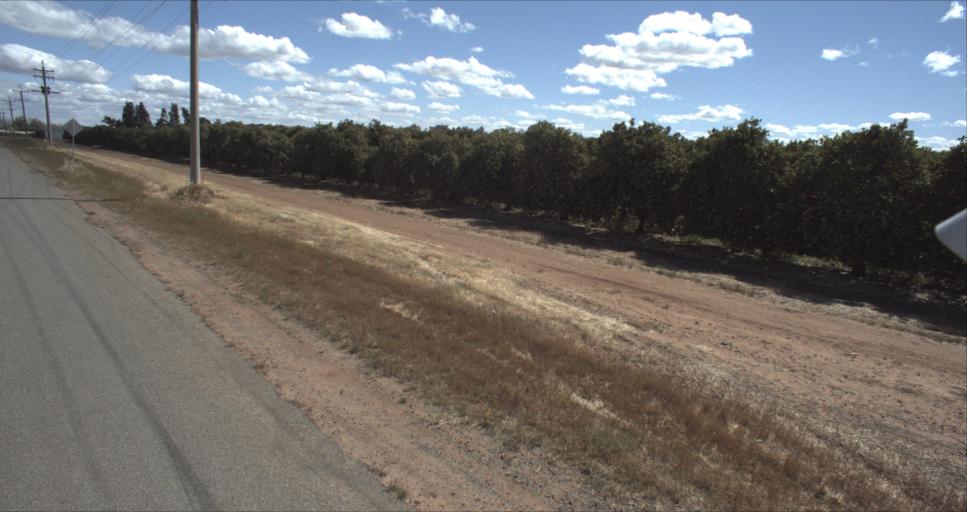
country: AU
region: New South Wales
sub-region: Leeton
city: Leeton
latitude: -34.5092
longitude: 146.2543
